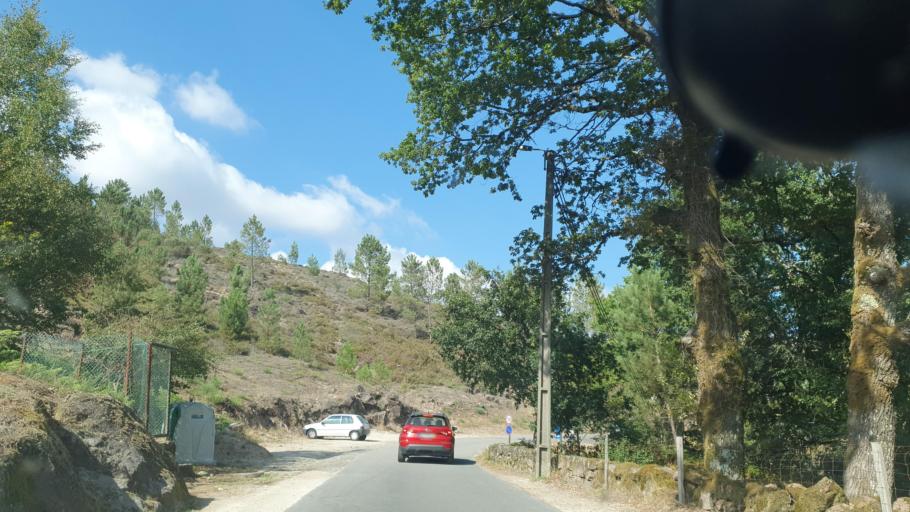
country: PT
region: Braga
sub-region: Terras de Bouro
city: Antas
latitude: 41.7627
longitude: -8.1913
